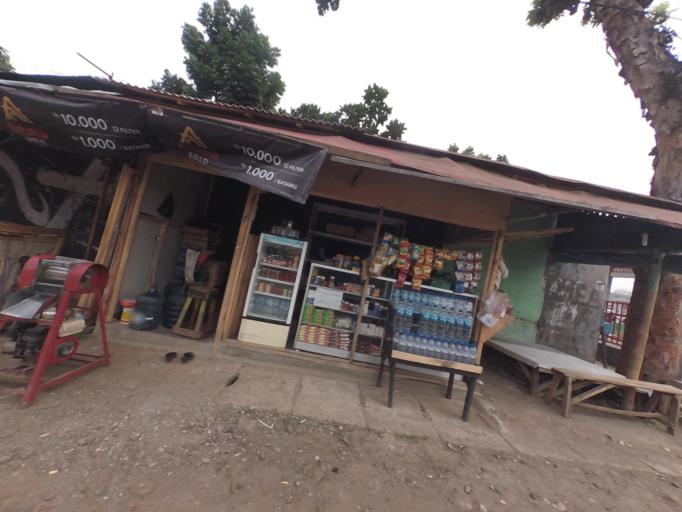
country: ID
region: West Java
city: Sidoger Lebak
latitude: -6.5665
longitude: 106.5983
